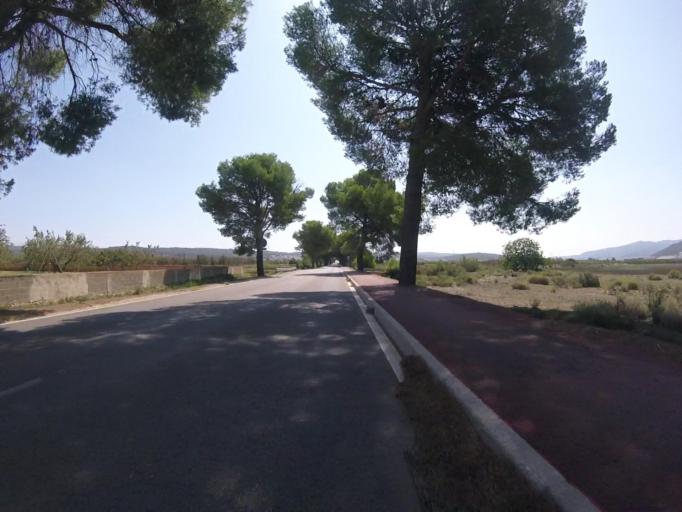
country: ES
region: Valencia
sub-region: Provincia de Castello
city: Cabanes
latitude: 40.1616
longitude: 0.0259
